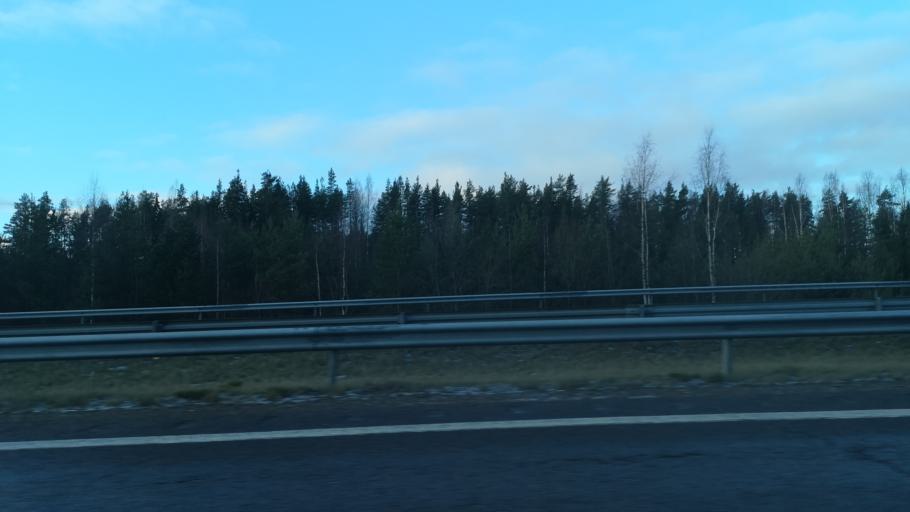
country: FI
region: Paijanne Tavastia
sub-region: Lahti
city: Heinola
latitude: 61.2819
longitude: 26.0700
